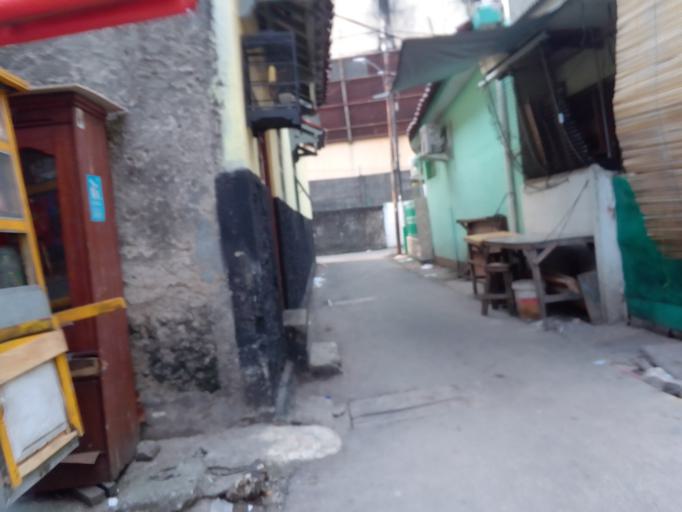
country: ID
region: Jakarta Raya
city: Jakarta
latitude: -6.1957
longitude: 106.8154
